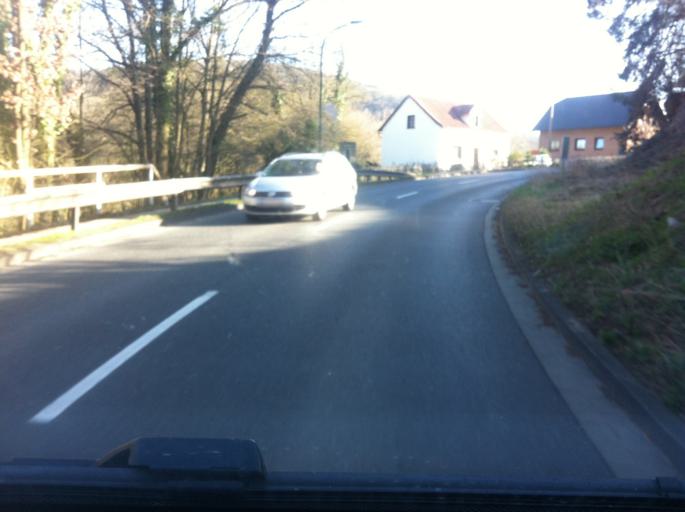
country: DE
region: North Rhine-Westphalia
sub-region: Regierungsbezirk Koln
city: Nideggen
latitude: 50.6873
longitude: 6.4712
